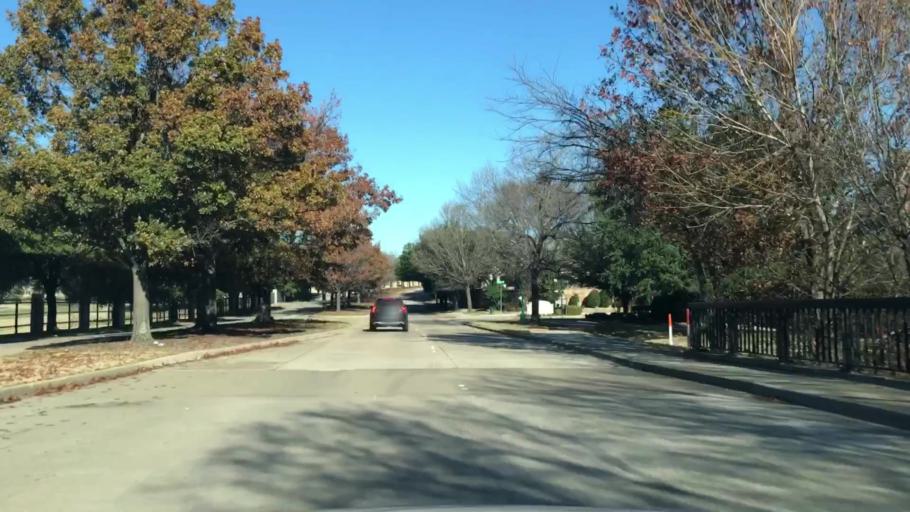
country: US
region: Texas
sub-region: Denton County
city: The Colony
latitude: 33.0947
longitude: -96.8406
